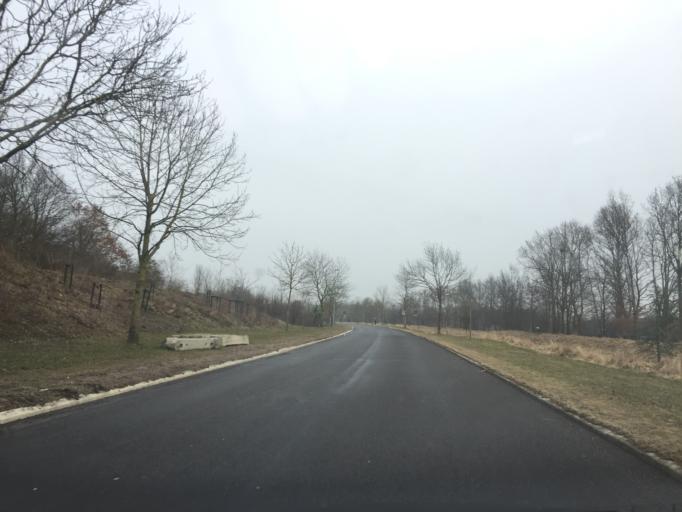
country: DK
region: Capital Region
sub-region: Hoje-Taastrup Kommune
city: Flong
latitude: 55.6474
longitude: 12.2129
